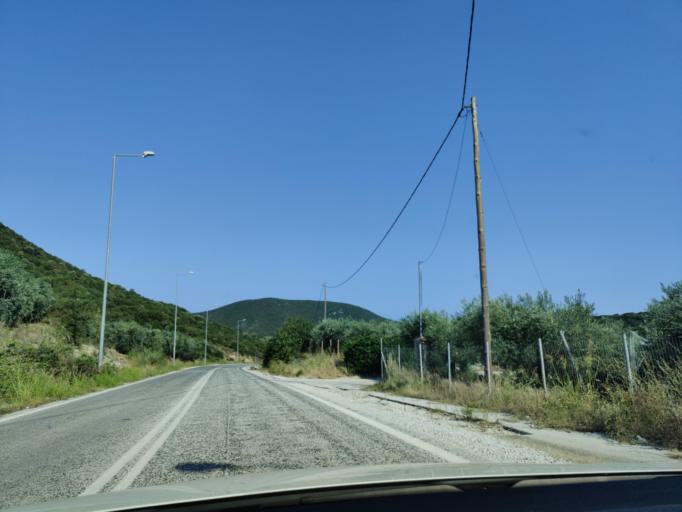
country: GR
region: East Macedonia and Thrace
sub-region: Nomos Kavalas
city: Nea Iraklitsa
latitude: 40.8590
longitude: 24.3055
